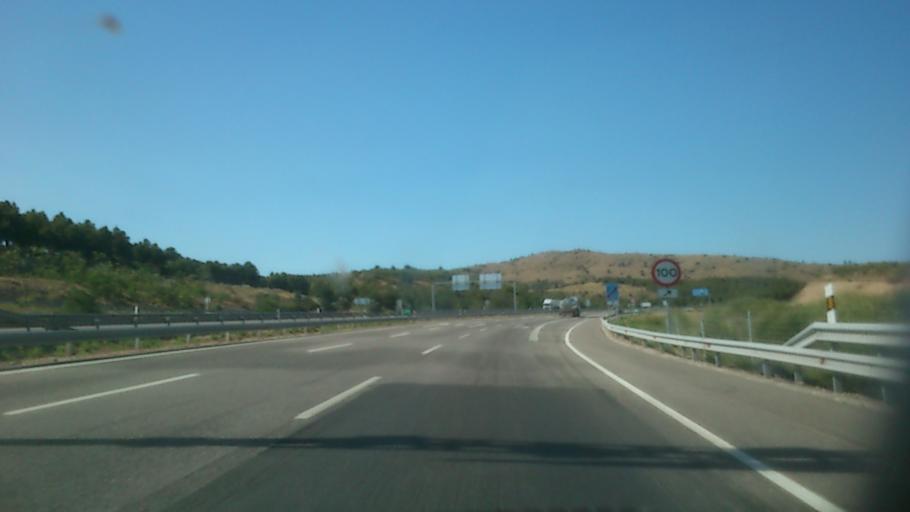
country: ES
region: Aragon
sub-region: Provincia de Zaragoza
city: Paracuellos de la Ribera
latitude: 41.3793
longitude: -1.5717
